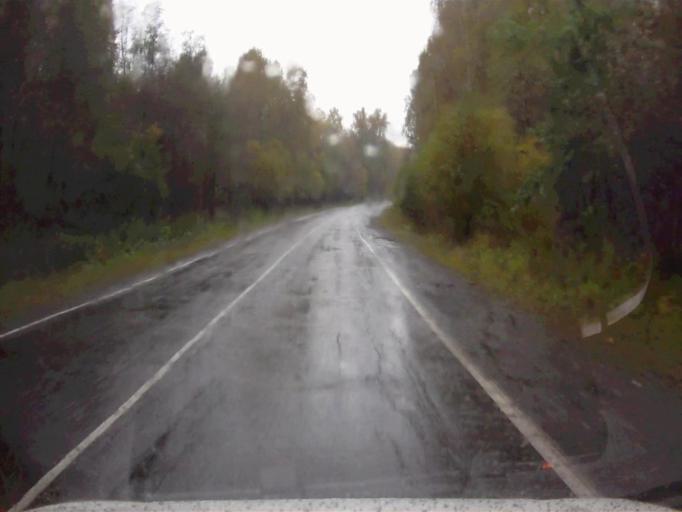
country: RU
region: Chelyabinsk
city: Kyshtym
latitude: 55.9110
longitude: 60.4334
